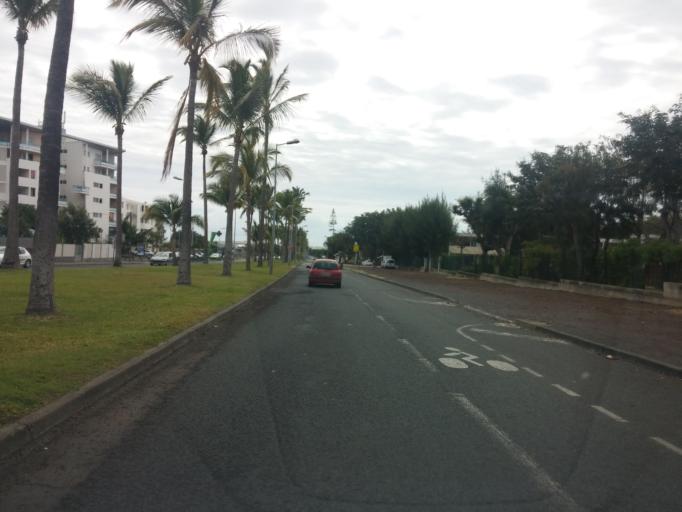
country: RE
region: Reunion
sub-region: Reunion
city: Le Port
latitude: -20.9467
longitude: 55.2934
